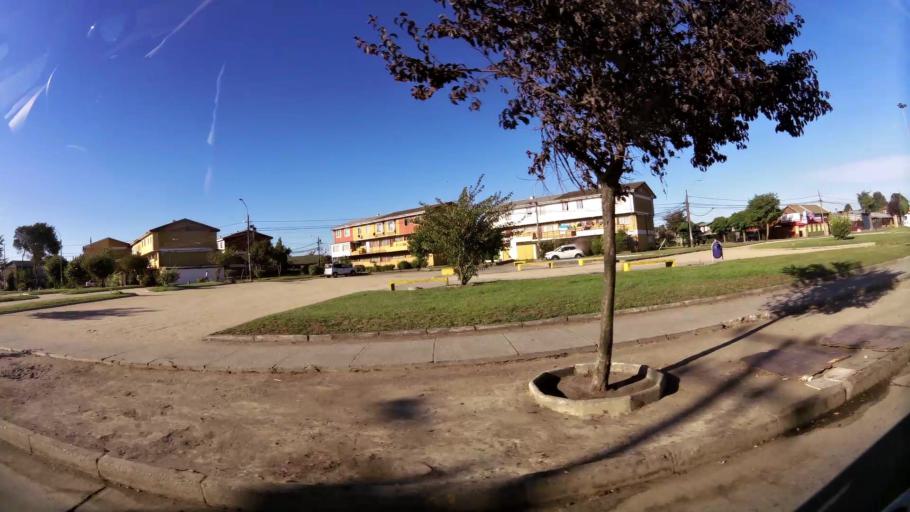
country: CL
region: Biobio
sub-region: Provincia de Concepcion
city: Concepcion
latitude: -36.8298
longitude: -73.1219
